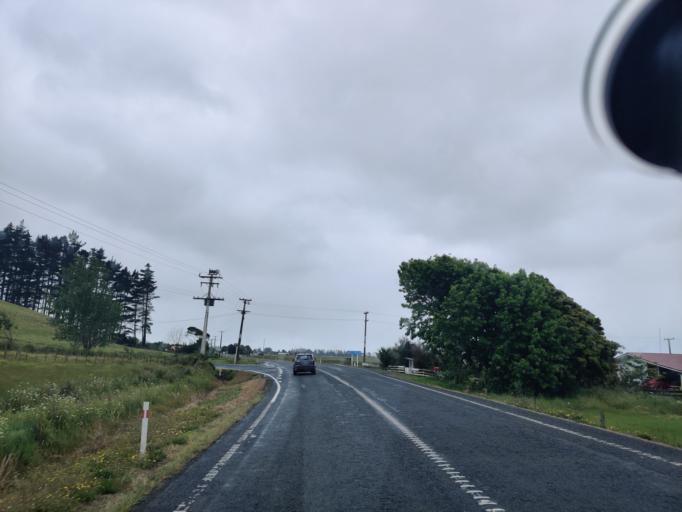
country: NZ
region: Northland
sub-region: Kaipara District
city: Dargaville
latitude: -35.9959
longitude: 173.9198
